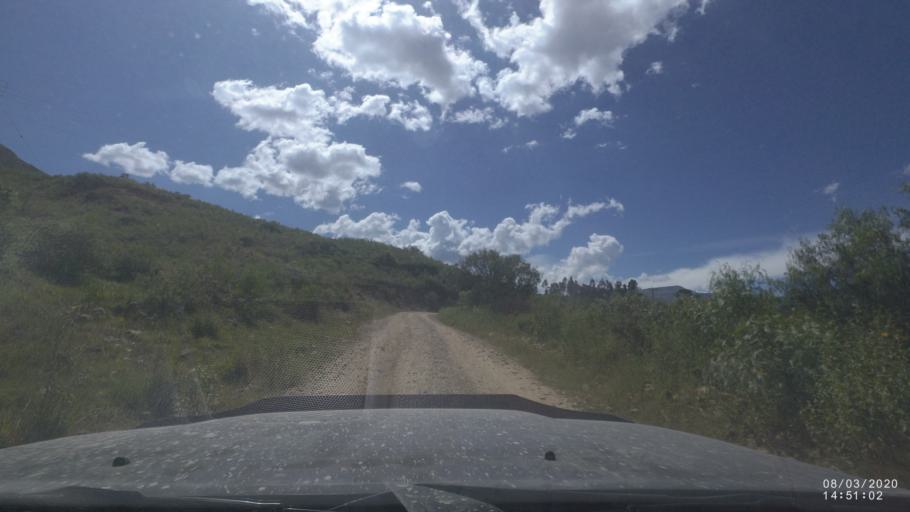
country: BO
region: Cochabamba
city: Totora
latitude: -17.6895
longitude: -65.3461
